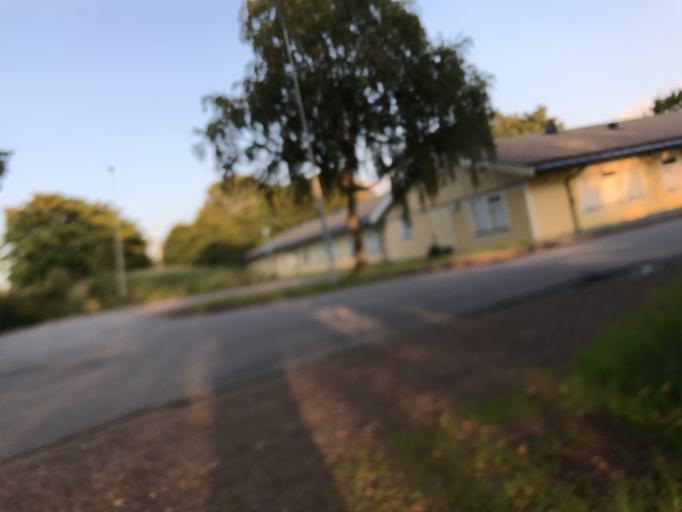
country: SE
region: Vaestra Goetaland
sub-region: Goteborg
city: Majorna
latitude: 57.7287
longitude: 11.8865
